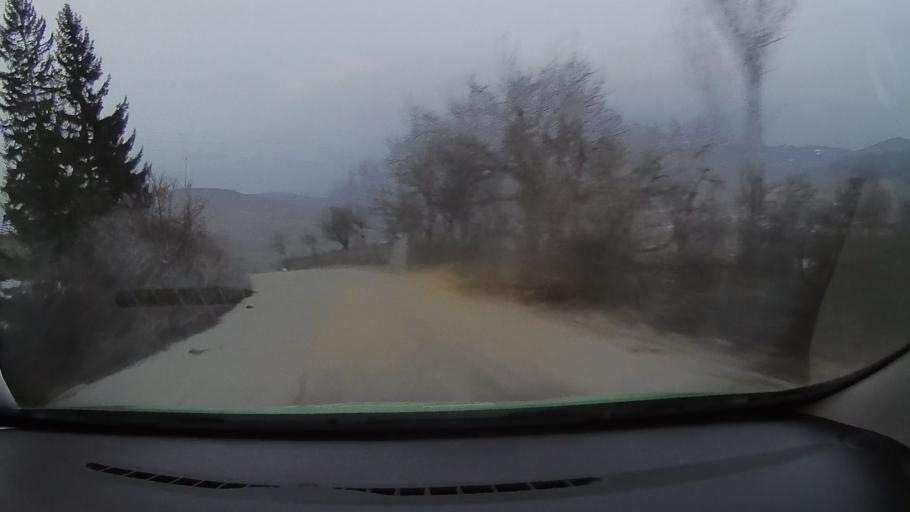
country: RO
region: Prahova
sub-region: Comuna Valea Doftanei
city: Tesila
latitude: 45.2953
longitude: 25.7134
